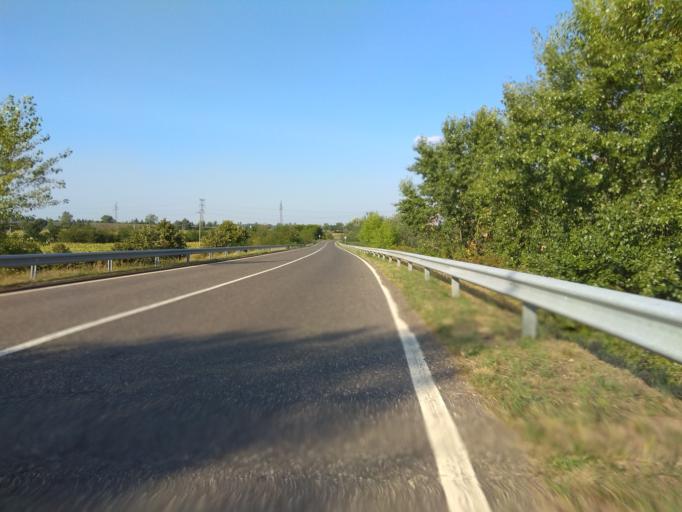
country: HU
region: Borsod-Abauj-Zemplen
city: Onod
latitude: 47.9728
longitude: 20.8994
